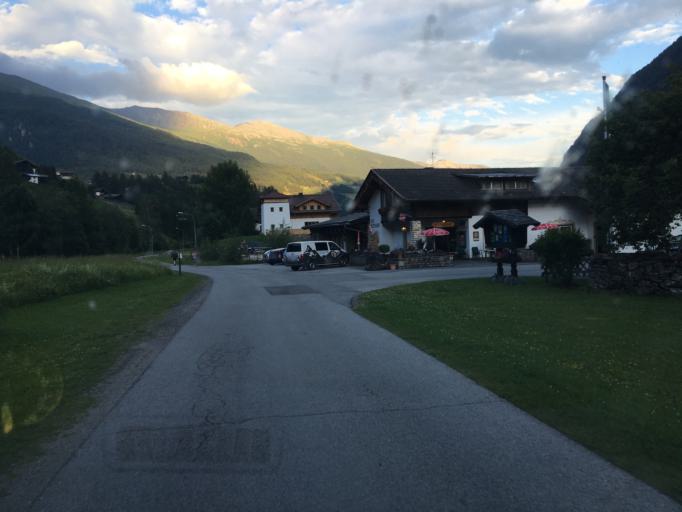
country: AT
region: Carinthia
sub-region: Politischer Bezirk Spittal an der Drau
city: Heiligenblut
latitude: 47.0376
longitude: 12.8389
